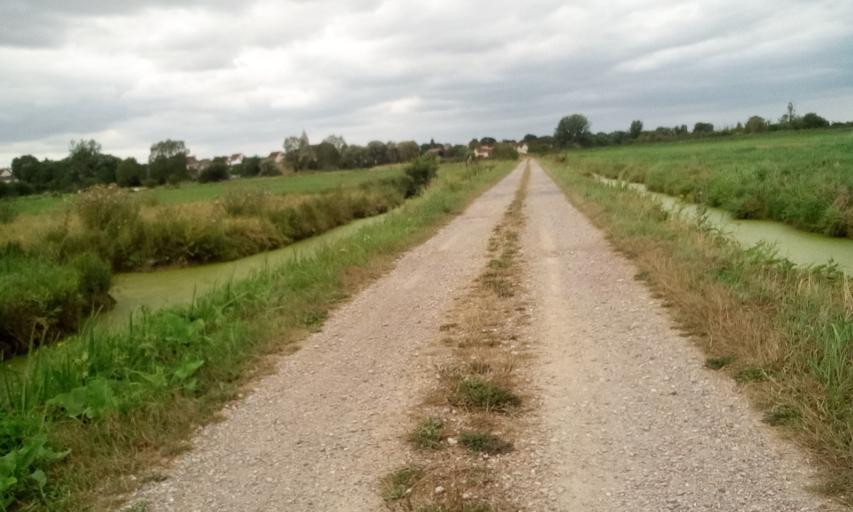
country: FR
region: Lower Normandy
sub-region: Departement du Calvados
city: Troarn
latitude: 49.1948
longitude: -0.1686
